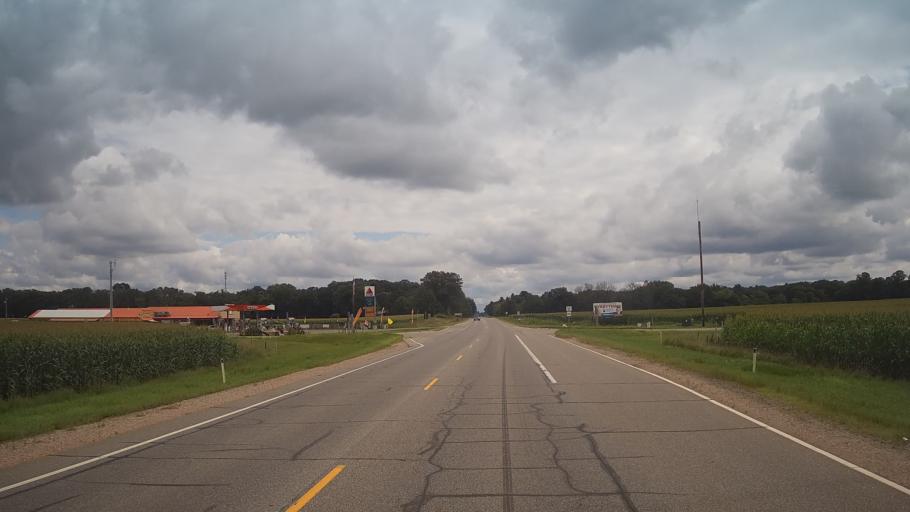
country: US
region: Wisconsin
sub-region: Adams County
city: Friendship
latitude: 44.0394
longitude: -89.9392
